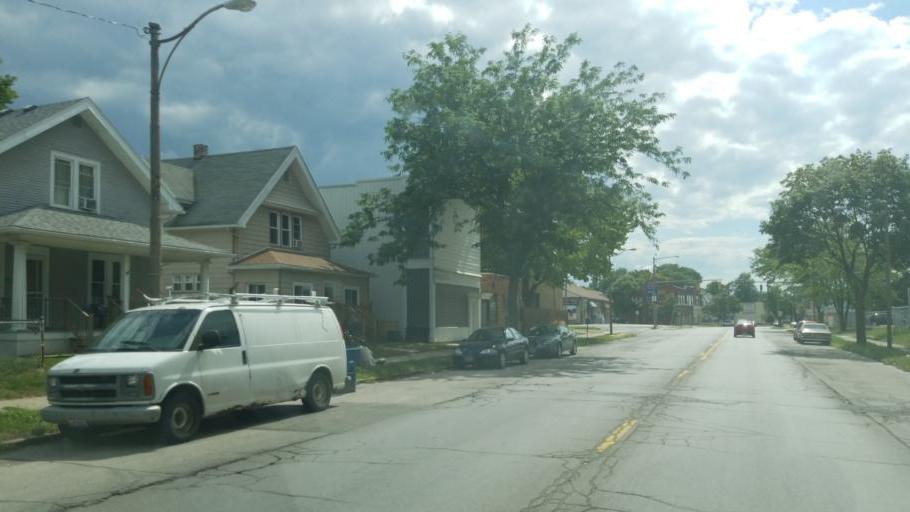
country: US
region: Ohio
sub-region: Wood County
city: Rossford
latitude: 41.6285
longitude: -83.5599
